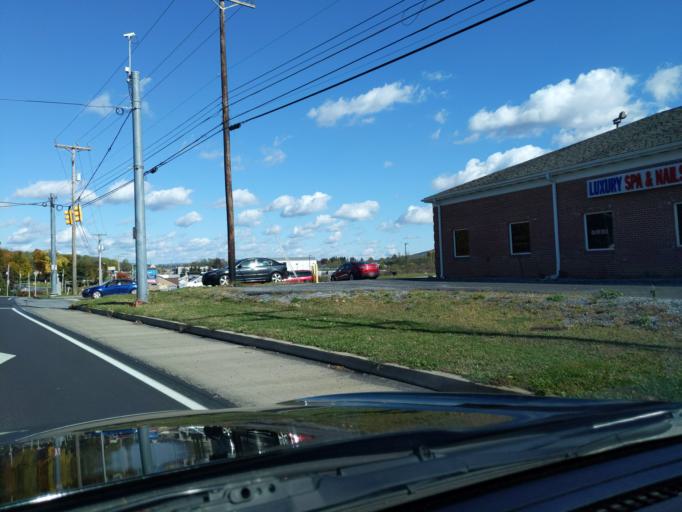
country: US
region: Pennsylvania
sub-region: Blair County
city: Lakemont
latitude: 40.4534
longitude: -78.4098
